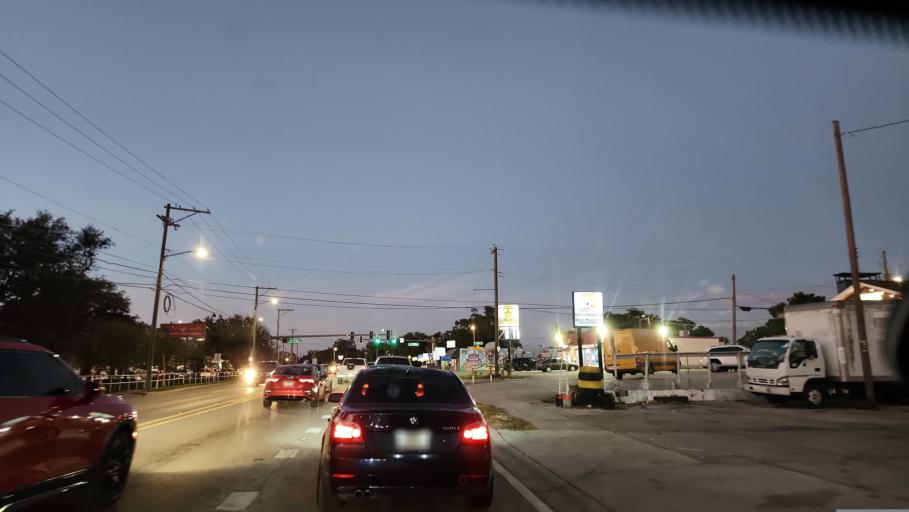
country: US
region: Florida
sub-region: Hillsborough County
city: Egypt Lake-Leto
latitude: 28.0096
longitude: -82.4843
